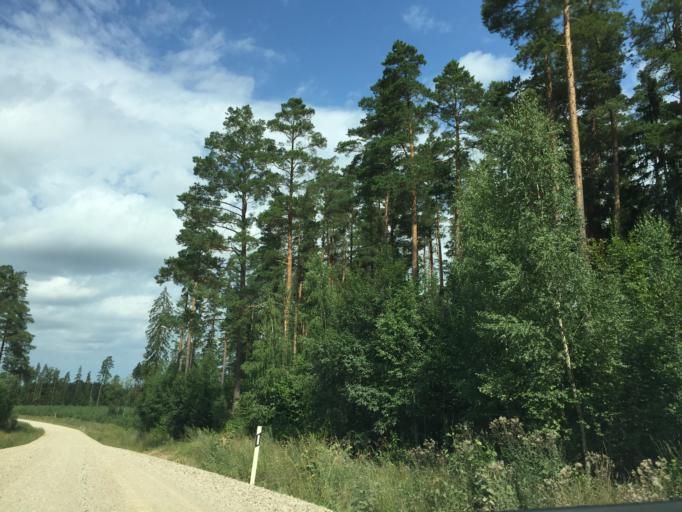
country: LV
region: Kandava
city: Kandava
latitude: 57.0179
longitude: 22.8275
